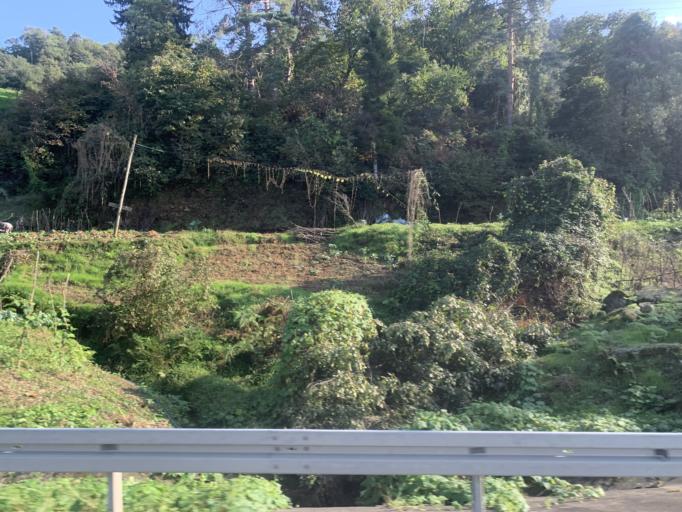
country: TR
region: Trabzon
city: Of
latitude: 40.9330
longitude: 40.2418
